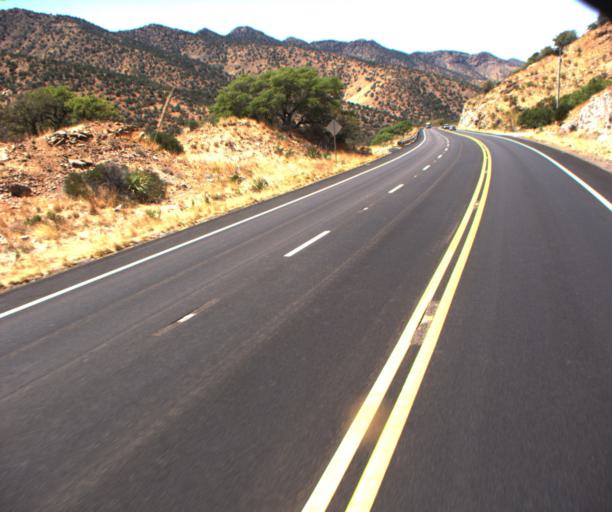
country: US
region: Arizona
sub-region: Cochise County
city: Bisbee
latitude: 31.4654
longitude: -109.9526
